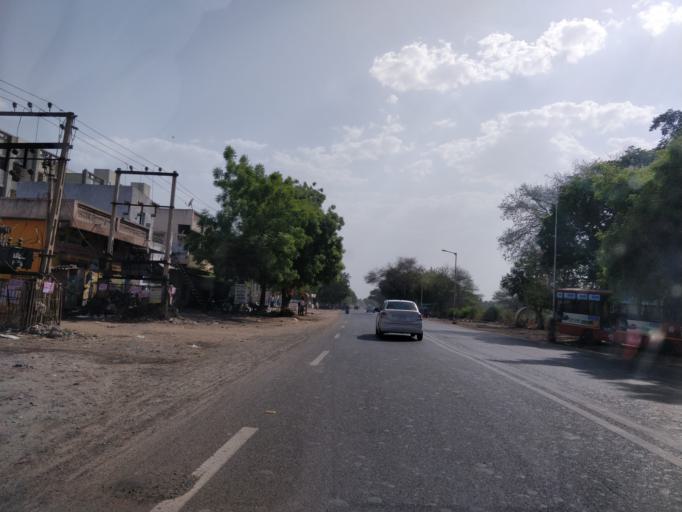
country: IN
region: Gujarat
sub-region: Ahmadabad
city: Naroda
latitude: 23.0792
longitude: 72.6677
